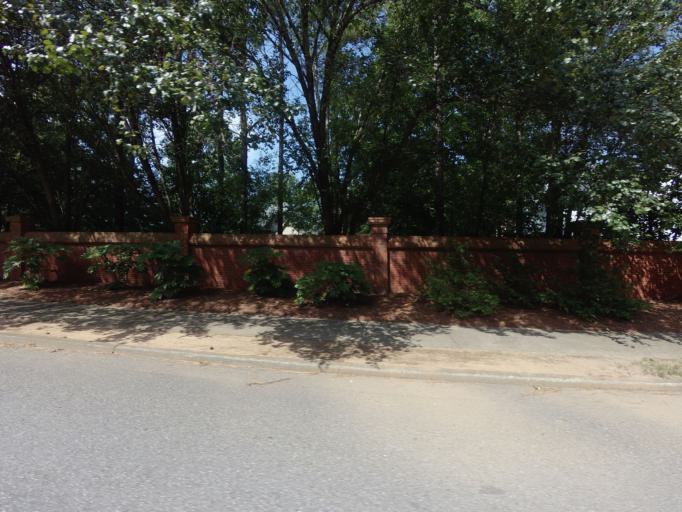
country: US
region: Georgia
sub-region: Fulton County
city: Johns Creek
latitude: 34.0333
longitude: -84.2347
